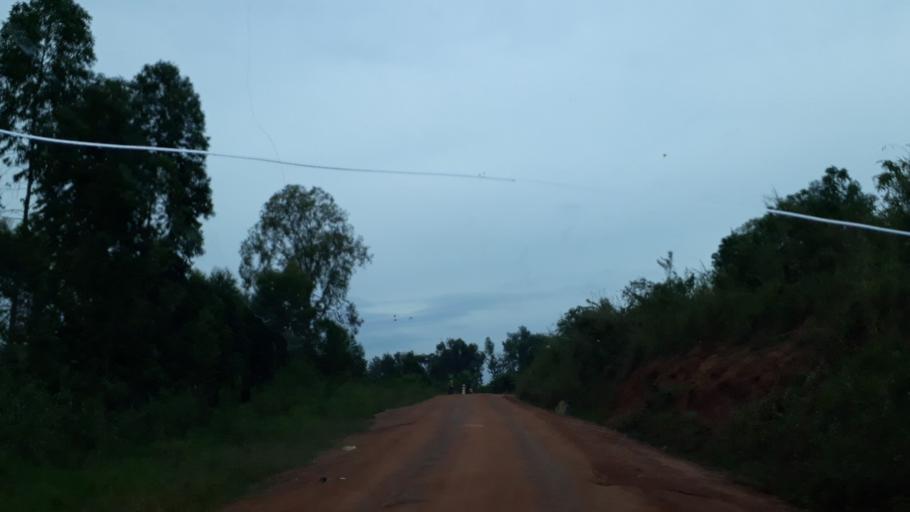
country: UG
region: Northern Region
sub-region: Zombo District
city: Paidha
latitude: 2.2179
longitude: 30.7797
